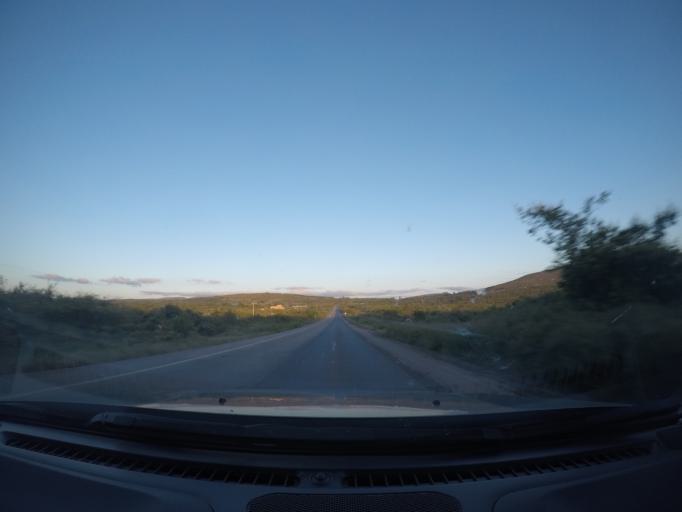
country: BR
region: Bahia
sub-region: Seabra
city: Seabra
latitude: -12.3902
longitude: -41.9003
